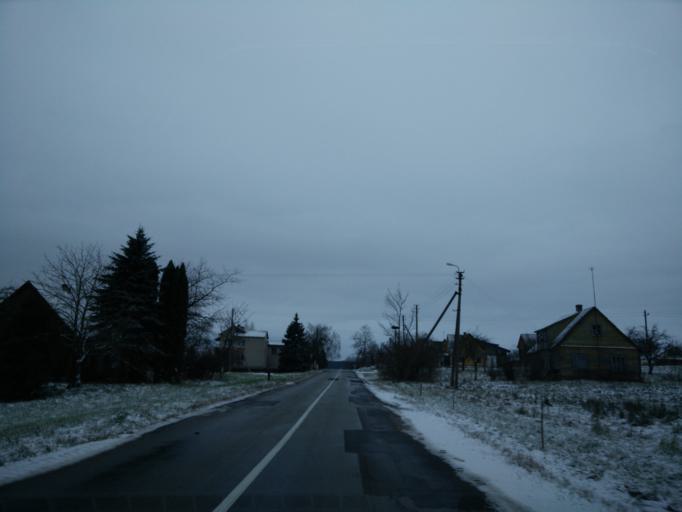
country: LT
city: Tytuveneliai
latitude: 55.4944
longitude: 23.3323
